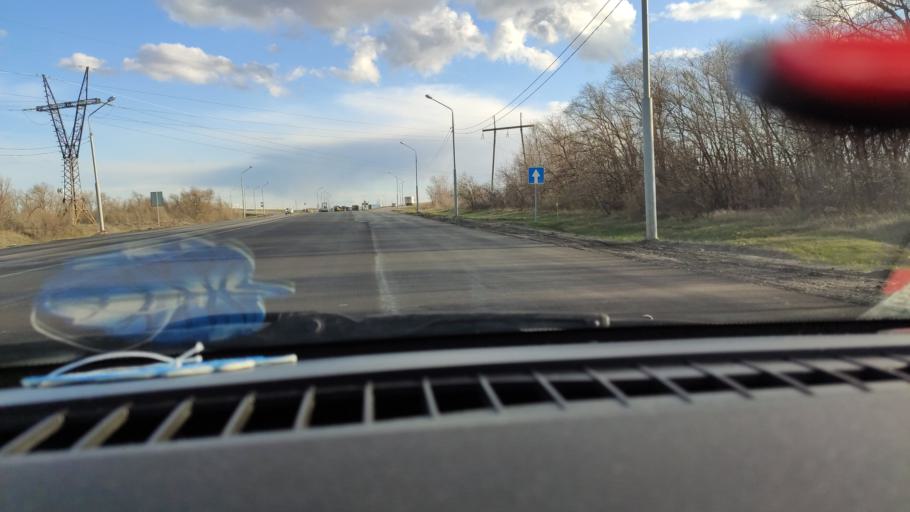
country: RU
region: Saratov
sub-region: Saratovskiy Rayon
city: Saratov
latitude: 51.6702
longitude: 45.9988
